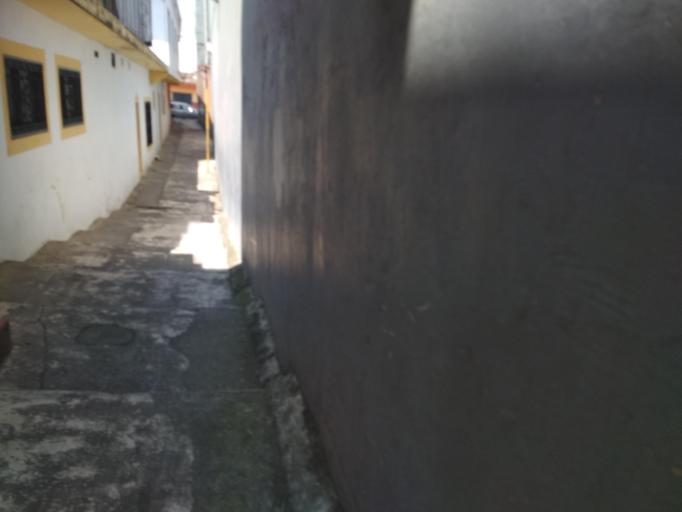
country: MX
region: Veracruz
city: Orizaba
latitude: 18.8404
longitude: -97.1114
